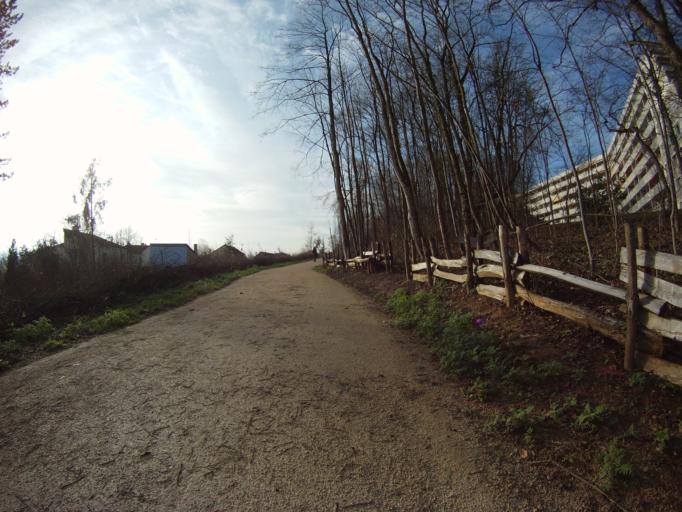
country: FR
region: Lorraine
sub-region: Departement de Meurthe-et-Moselle
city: Saint-Max
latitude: 48.7090
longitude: 6.2020
